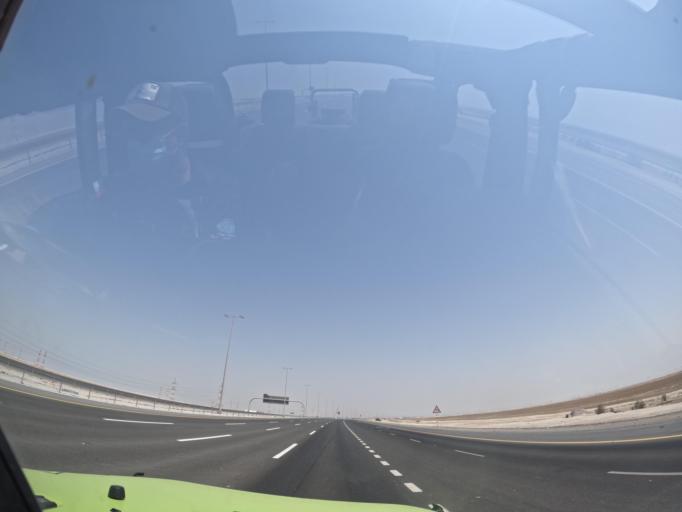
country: AE
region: Abu Dhabi
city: Abu Dhabi
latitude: 24.1522
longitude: 54.2494
